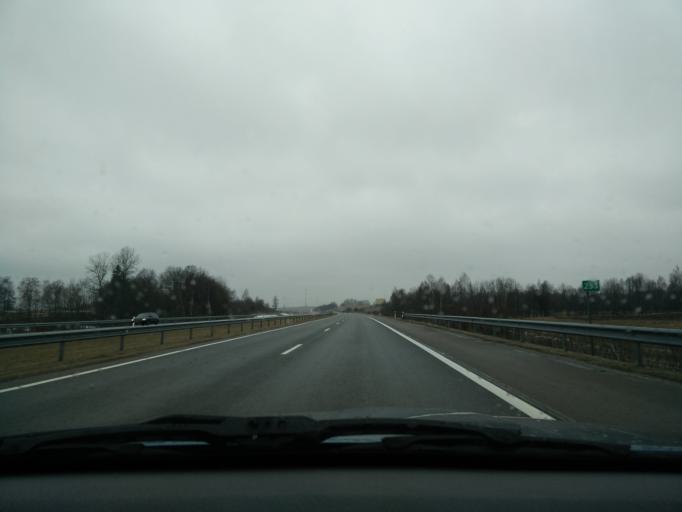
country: LT
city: Silale
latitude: 55.5527
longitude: 22.2607
